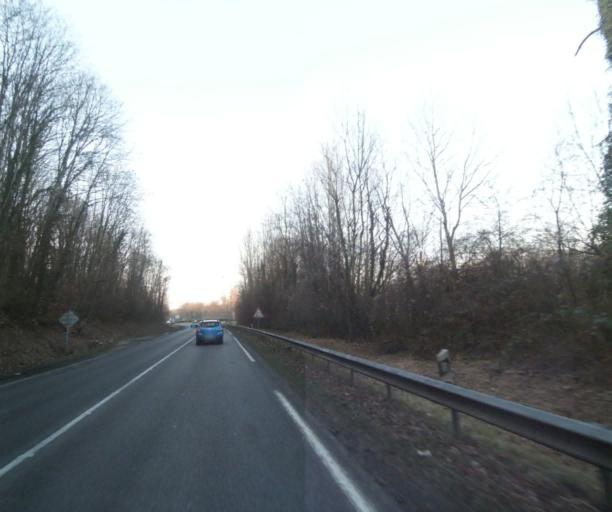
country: FR
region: Lorraine
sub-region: Departement de la Meuse
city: Ancerville
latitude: 48.6214
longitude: 4.9943
